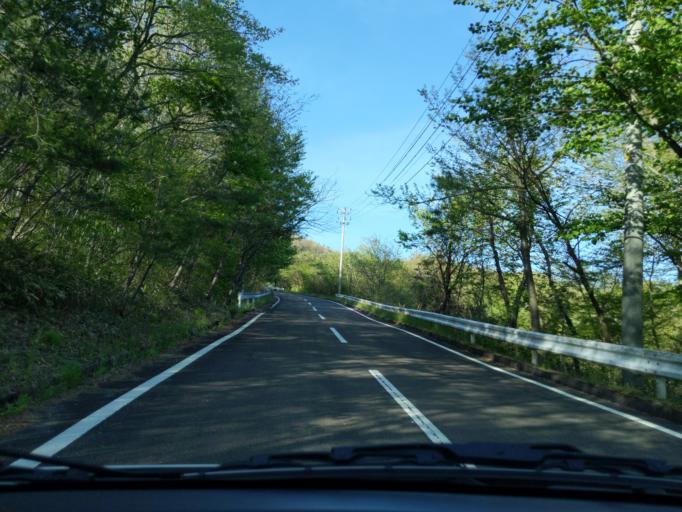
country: JP
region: Iwate
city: Ichinoseki
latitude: 38.8786
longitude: 140.9105
